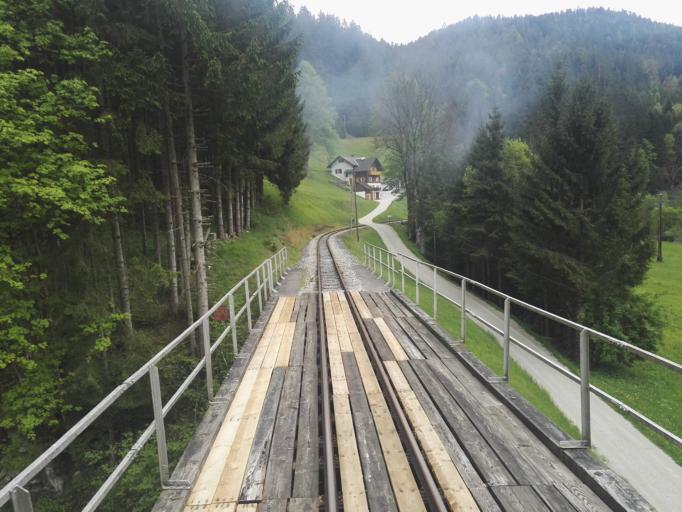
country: AT
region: Styria
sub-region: Politischer Bezirk Weiz
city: Birkfeld
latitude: 47.3414
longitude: 15.7010
